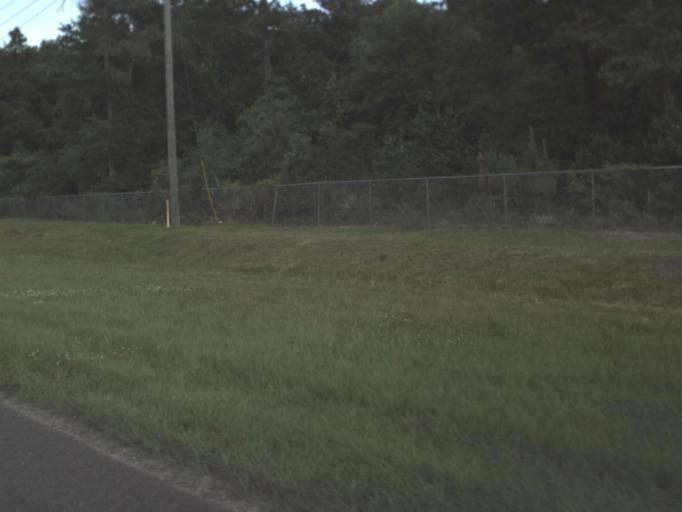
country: US
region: Florida
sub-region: Saint Johns County
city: Saint Augustine Shores
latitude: 29.7749
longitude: -81.4521
